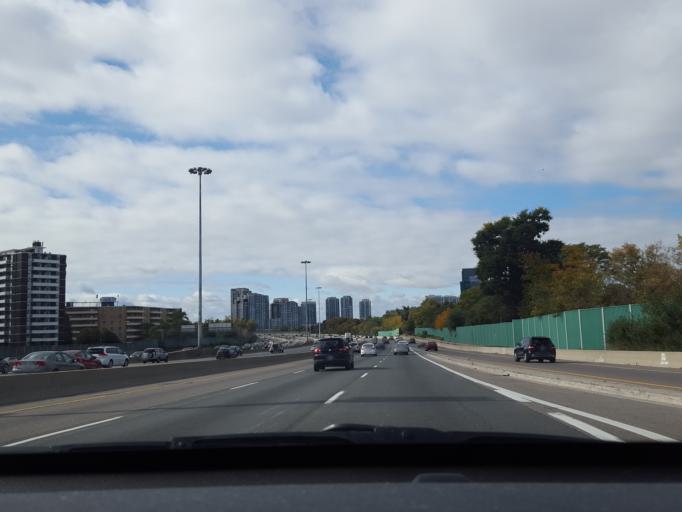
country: CA
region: Ontario
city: Willowdale
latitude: 43.7631
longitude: -79.3892
